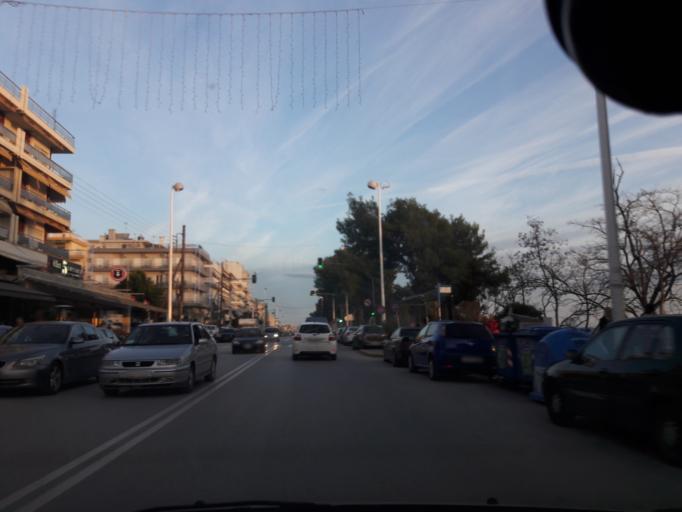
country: GR
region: Central Macedonia
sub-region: Nomos Thessalonikis
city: Kalamaria
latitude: 40.5759
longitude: 22.9470
